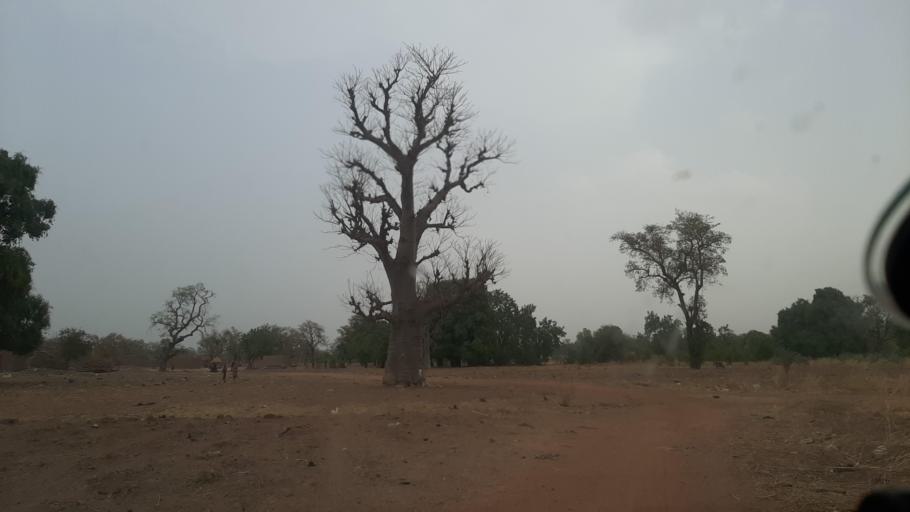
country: BF
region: Boucle du Mouhoun
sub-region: Province des Banwa
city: Salanso
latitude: 11.8700
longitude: -4.4488
